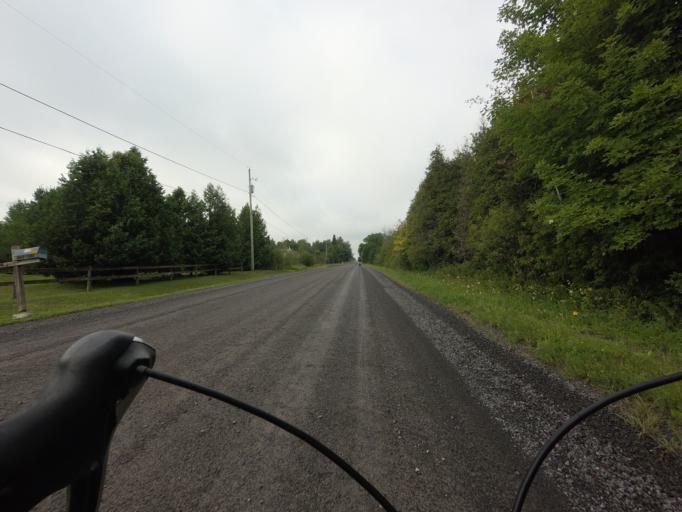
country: CA
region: Ontario
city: Bells Corners
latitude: 45.0387
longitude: -75.7441
